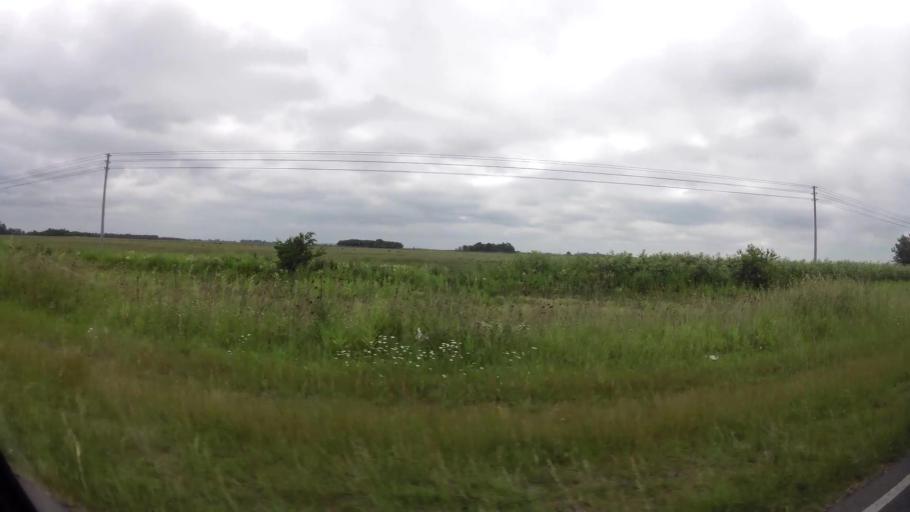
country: AR
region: Buenos Aires
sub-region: Partido de San Vicente
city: San Vicente
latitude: -35.0225
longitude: -58.4639
